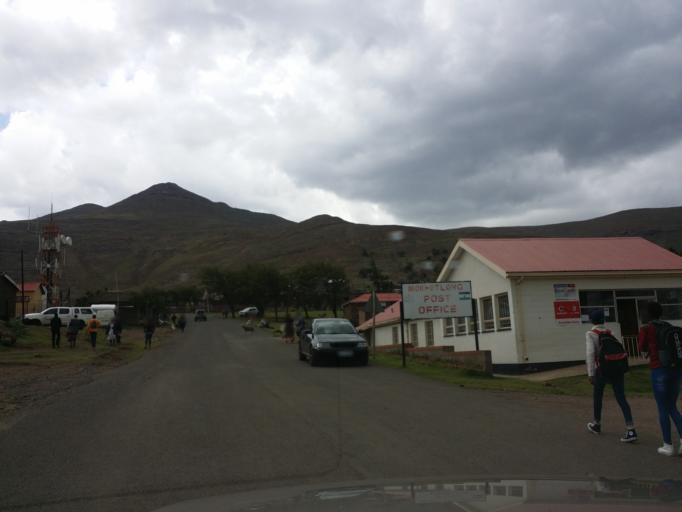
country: LS
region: Mokhotlong
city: Mokhotlong
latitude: -29.2887
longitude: 29.0691
